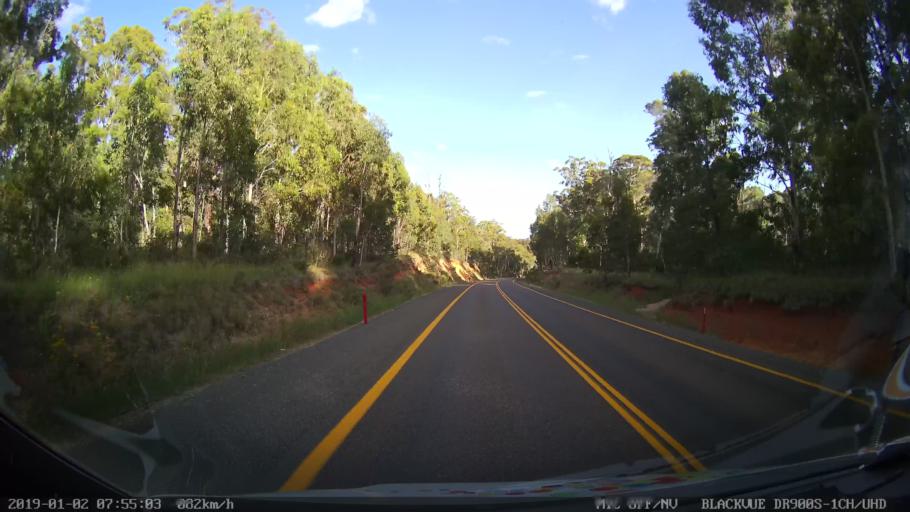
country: AU
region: New South Wales
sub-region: Tumut Shire
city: Tumut
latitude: -35.6897
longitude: 148.4900
